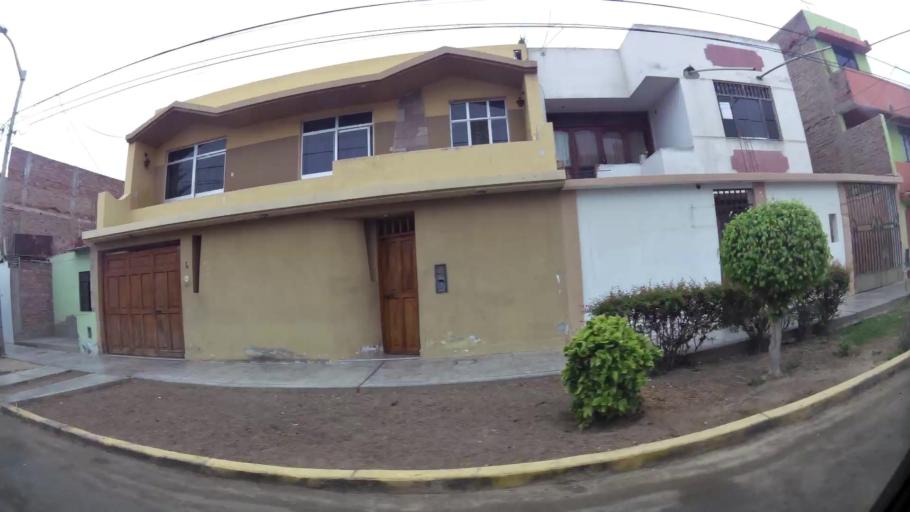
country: PE
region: La Libertad
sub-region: Provincia de Trujillo
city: Trujillo
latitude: -8.1110
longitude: -79.0406
